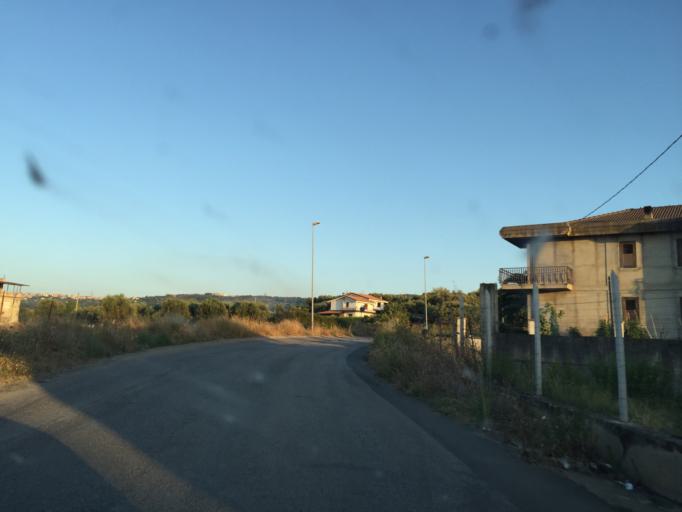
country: IT
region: Calabria
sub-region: Provincia di Vibo-Valentia
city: Pannaconi
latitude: 38.6979
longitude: 16.0463
